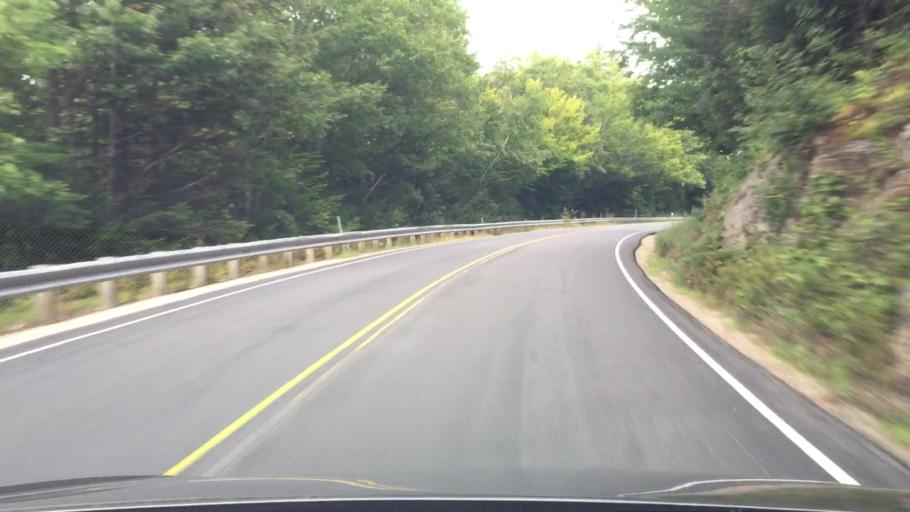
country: US
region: New Hampshire
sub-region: Carroll County
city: Conway
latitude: 43.9904
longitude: -71.1759
